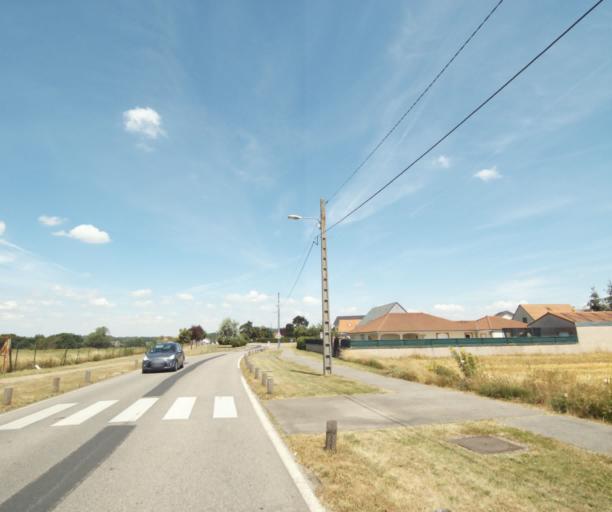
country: FR
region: Lorraine
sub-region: Departement de Meurthe-et-Moselle
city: Chanteheux
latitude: 48.5941
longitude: 6.5192
